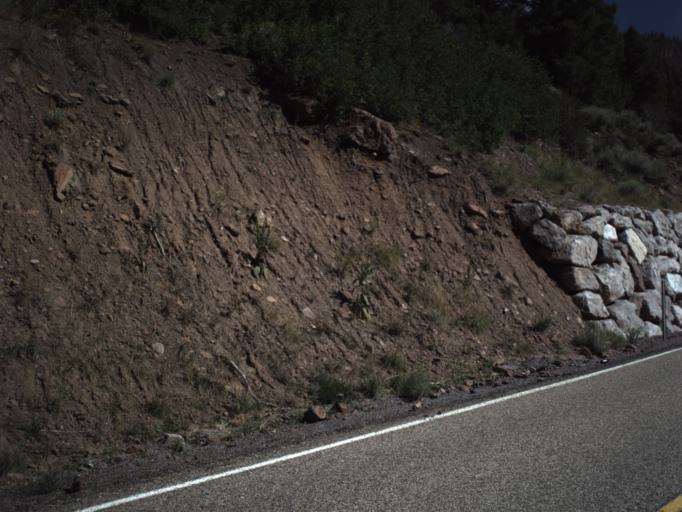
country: US
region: Utah
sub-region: Beaver County
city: Beaver
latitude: 38.2779
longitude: -112.4589
